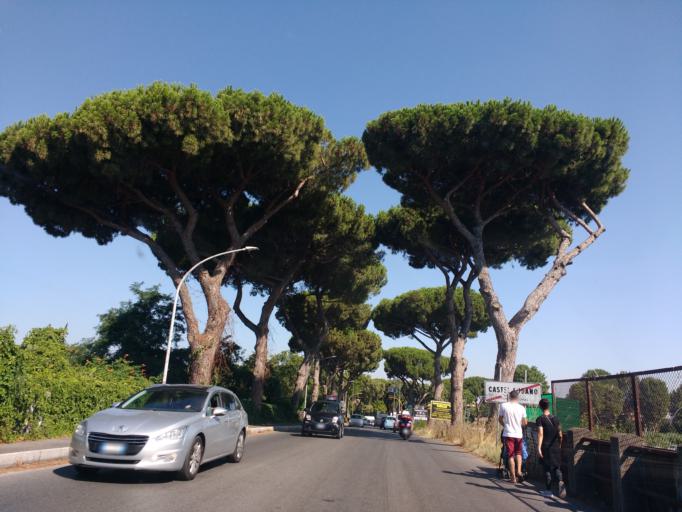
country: IT
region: Latium
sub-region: Citta metropolitana di Roma Capitale
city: Acilia-Castel Fusano-Ostia Antica
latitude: 41.7582
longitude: 12.3050
